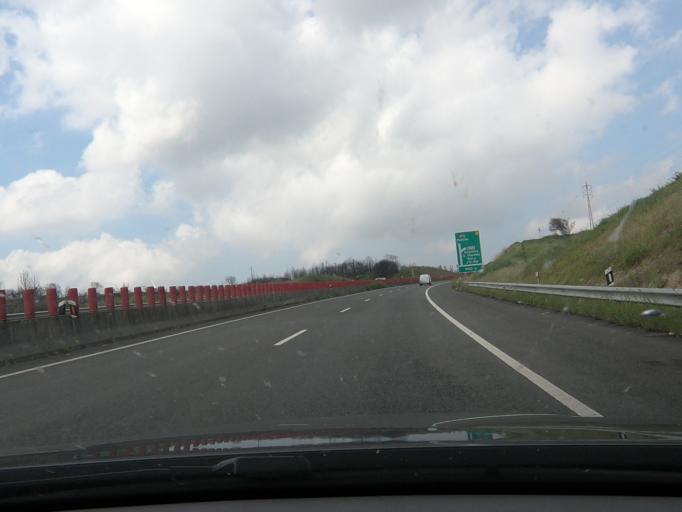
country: PT
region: Leiria
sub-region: Peniche
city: Atouguia da Baleia
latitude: 39.3328
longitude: -9.2436
